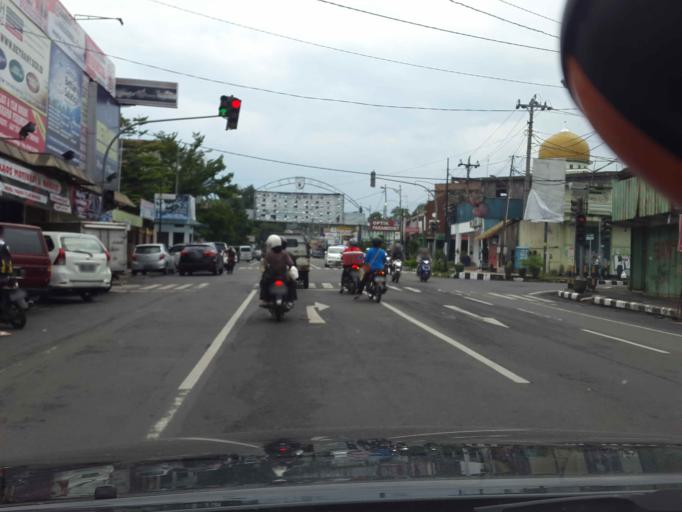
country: ID
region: Central Java
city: Salatiga
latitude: -7.3324
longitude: 110.5052
